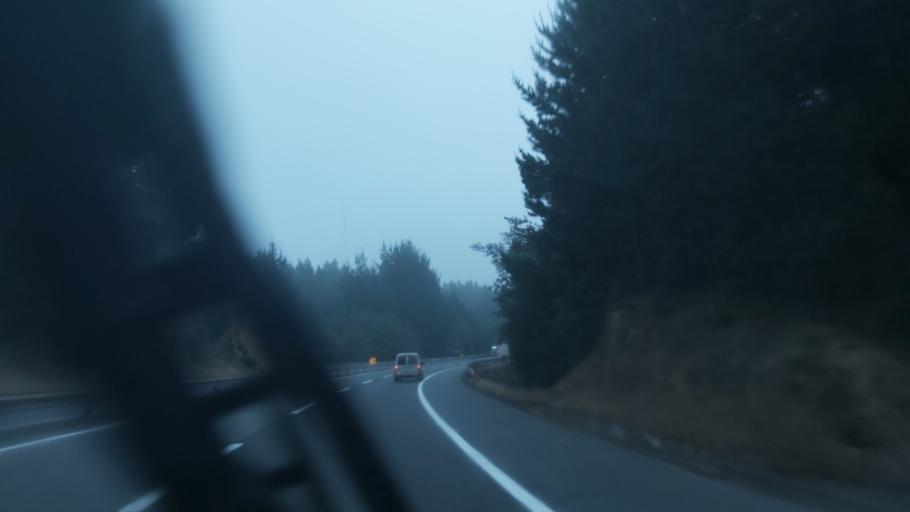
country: CL
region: Biobio
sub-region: Provincia de Concepcion
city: Penco
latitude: -36.7416
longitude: -72.9040
